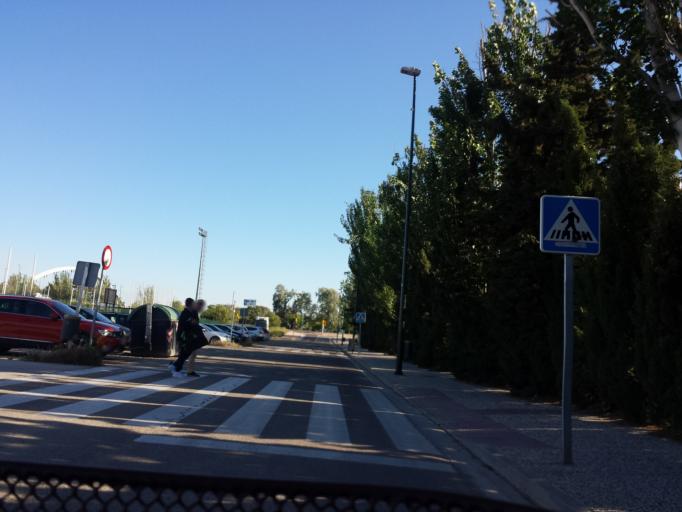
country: ES
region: Aragon
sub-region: Provincia de Zaragoza
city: Zaragoza
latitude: 41.6540
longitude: -0.8558
